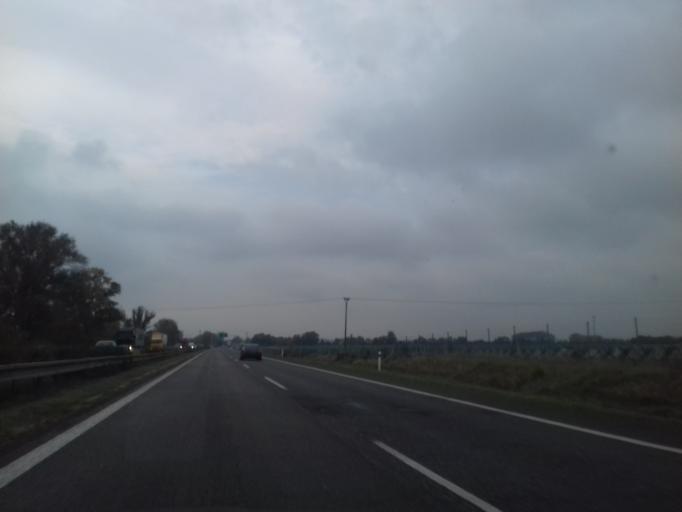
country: SK
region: Bratislavsky
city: Stupava
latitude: 48.2255
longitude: 17.0255
